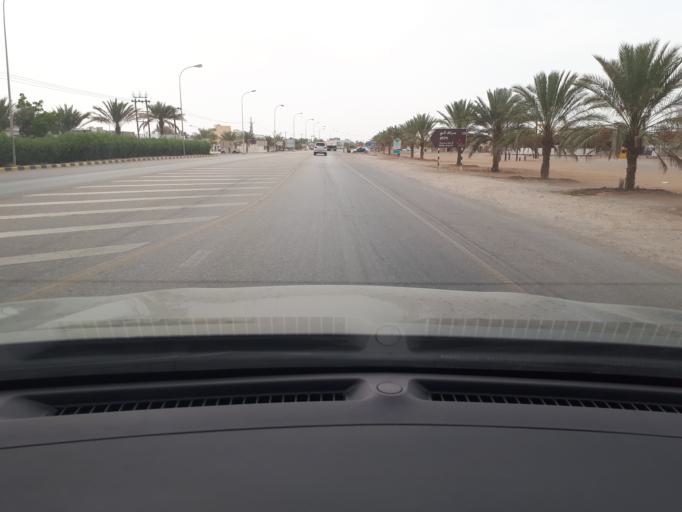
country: OM
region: Ash Sharqiyah
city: Badiyah
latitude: 22.4524
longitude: 58.8108
